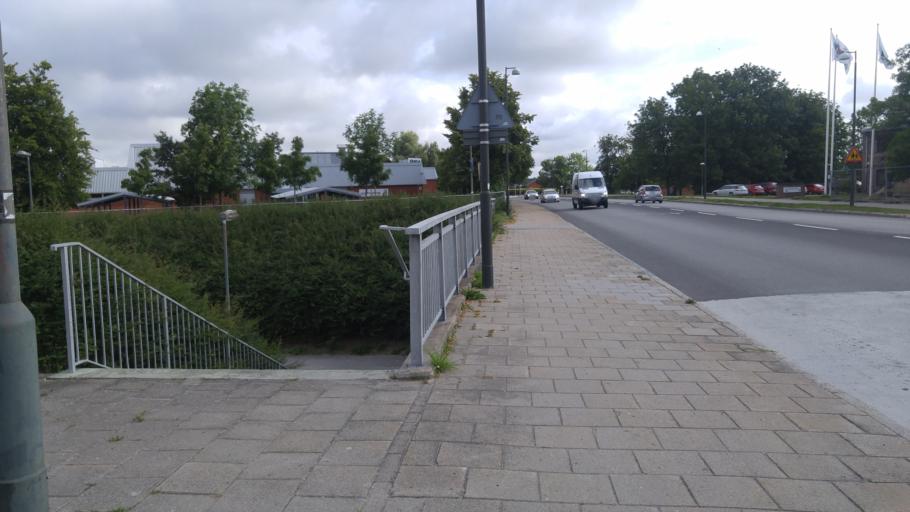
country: SE
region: Skane
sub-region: Burlovs Kommun
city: Arloev
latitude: 55.5820
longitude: 13.0658
